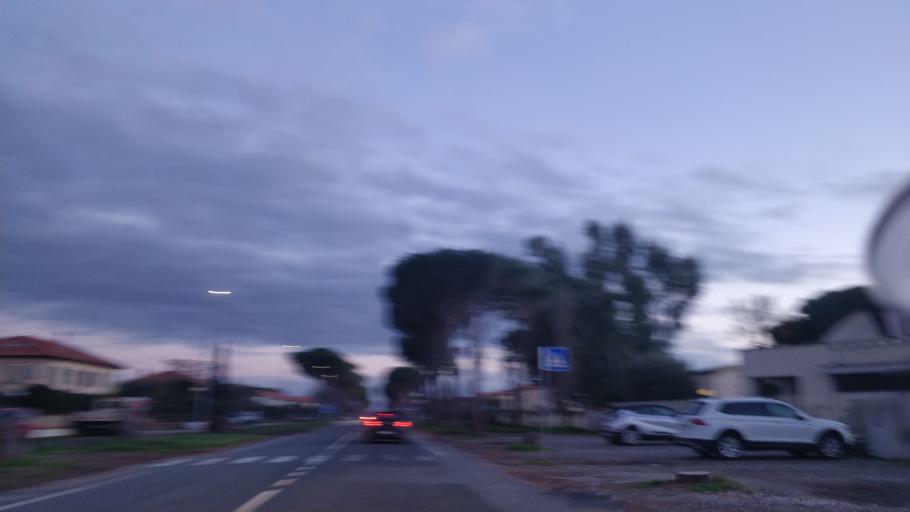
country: IT
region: Tuscany
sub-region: Provincia di Livorno
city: Rosignano Solvay-Castiglioncello
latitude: 43.3853
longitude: 10.4368
